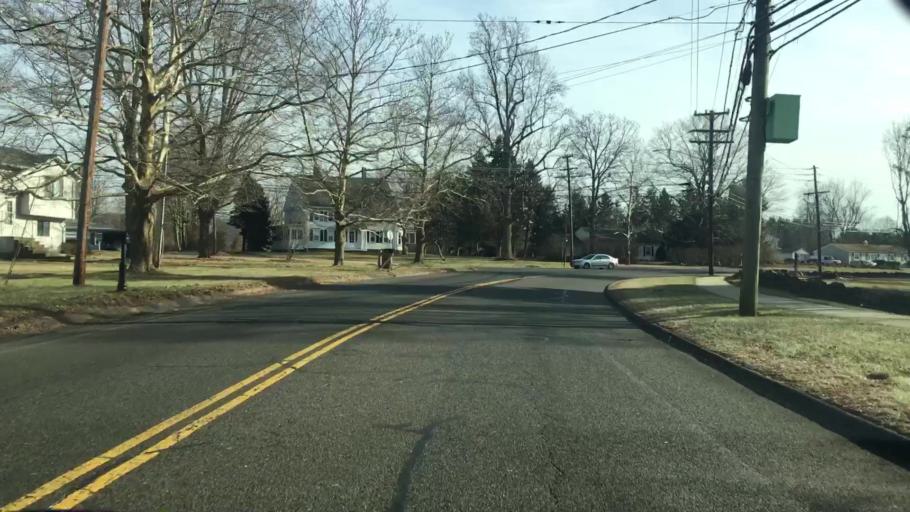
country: US
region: Connecticut
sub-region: New Haven County
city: Meriden
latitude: 41.5059
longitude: -72.7762
